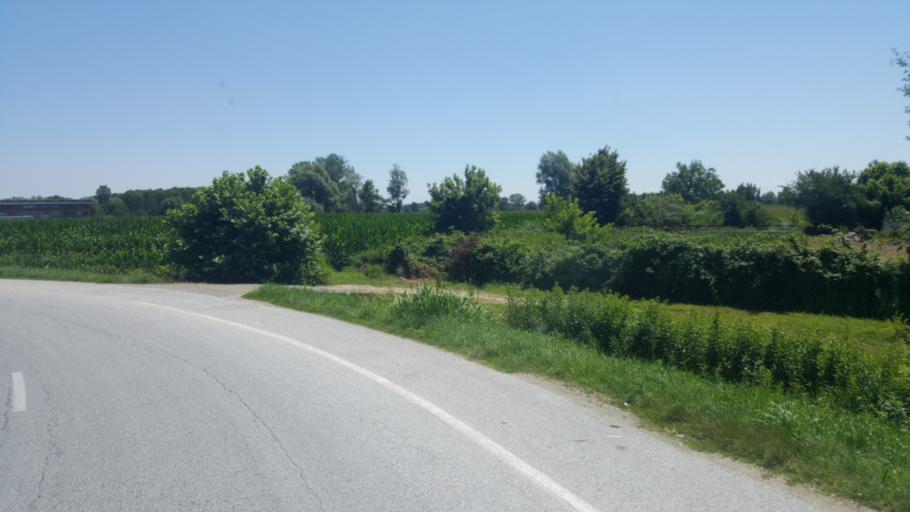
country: IT
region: Piedmont
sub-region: Provincia di Torino
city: Airasca
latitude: 44.9188
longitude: 7.4956
